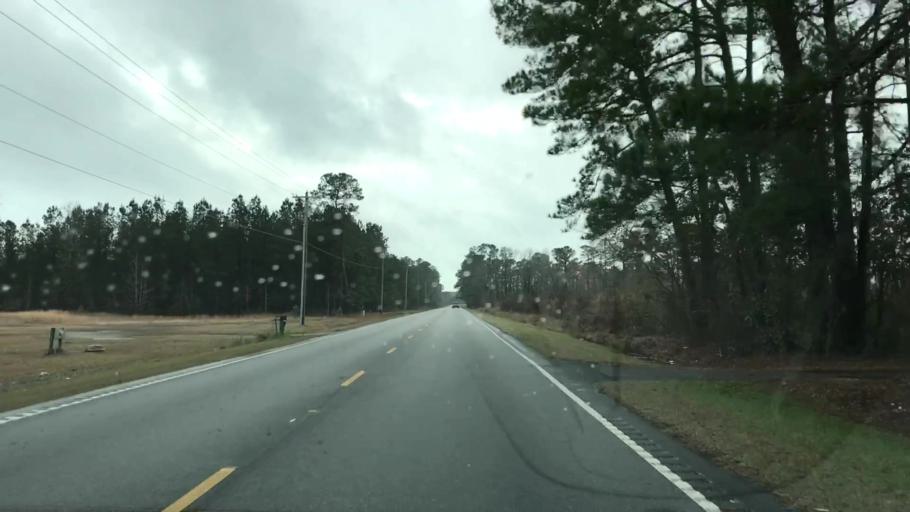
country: US
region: South Carolina
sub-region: Horry County
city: Socastee
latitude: 33.7334
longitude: -79.0827
